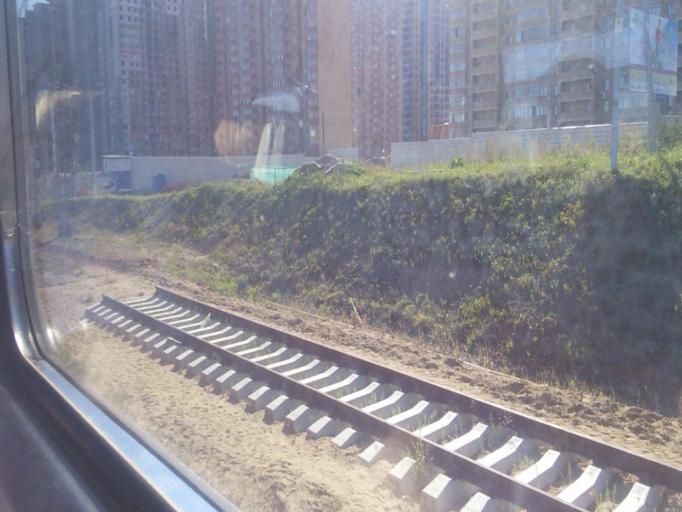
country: RU
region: Moskovskaya
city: Reutov
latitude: 55.7555
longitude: 37.8763
